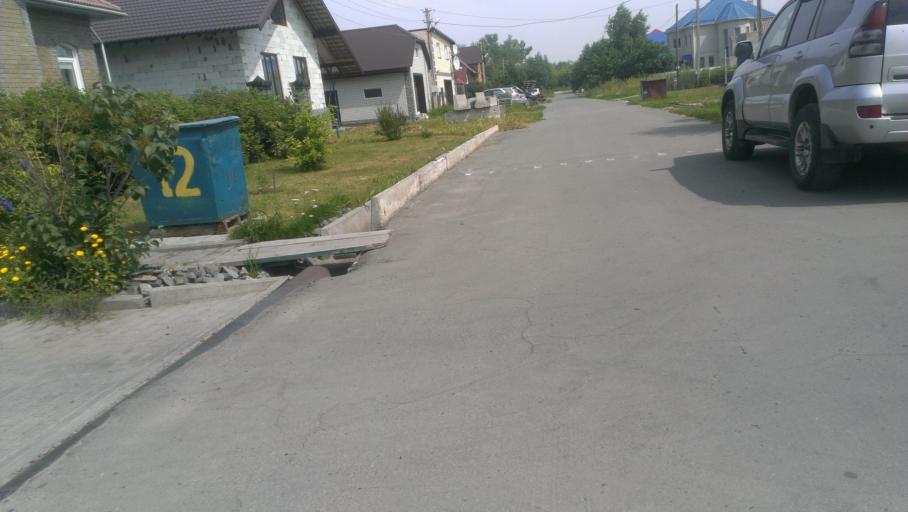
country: RU
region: Altai Krai
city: Novosilikatnyy
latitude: 53.3489
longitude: 83.6437
